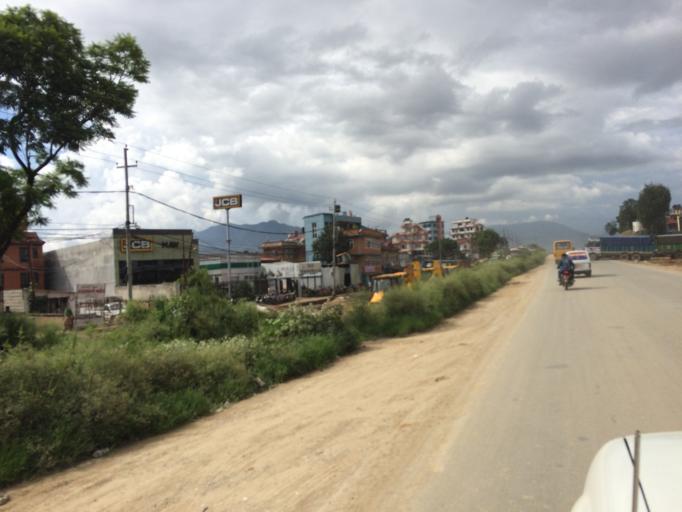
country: NP
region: Central Region
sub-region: Bagmati Zone
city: Patan
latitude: 27.6767
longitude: 85.3021
